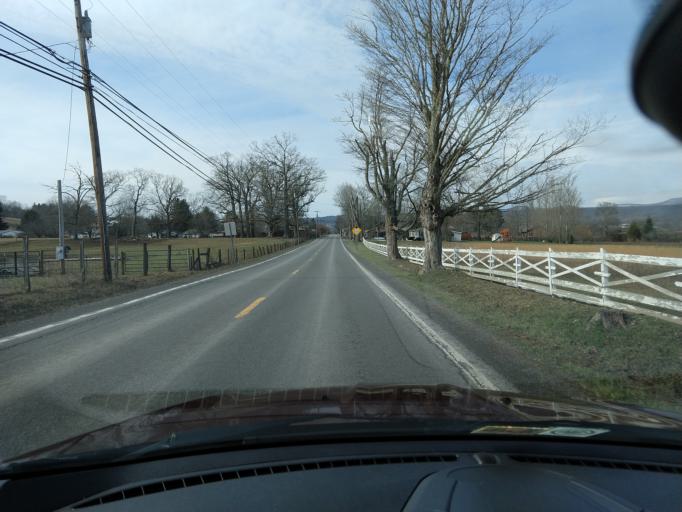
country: US
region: West Virginia
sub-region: Pocahontas County
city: Marlinton
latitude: 38.1405
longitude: -80.2047
